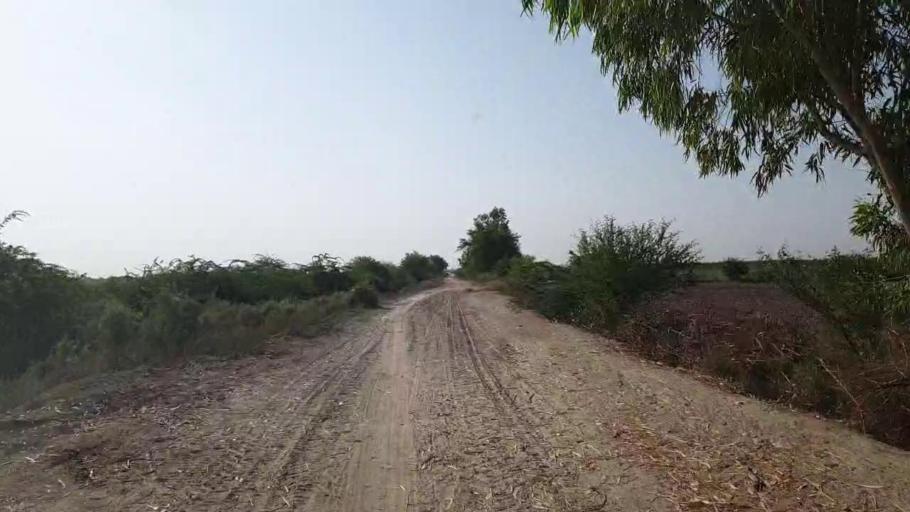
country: PK
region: Sindh
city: Kadhan
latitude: 24.6169
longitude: 69.0730
